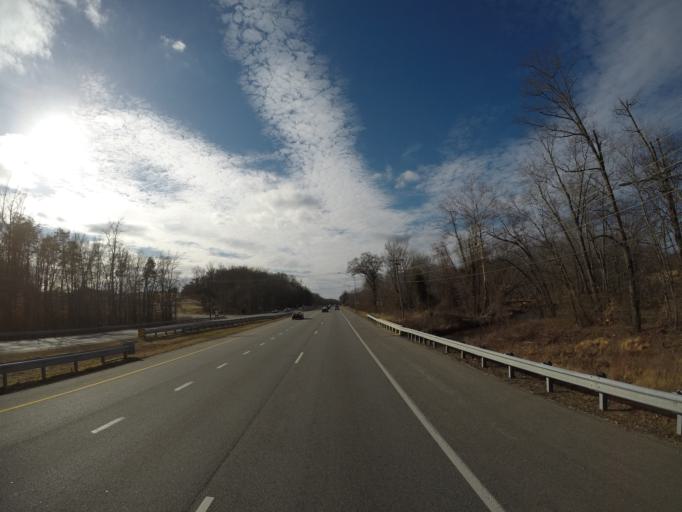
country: US
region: Maryland
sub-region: Charles County
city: Waldorf
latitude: 38.6526
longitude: -76.9776
